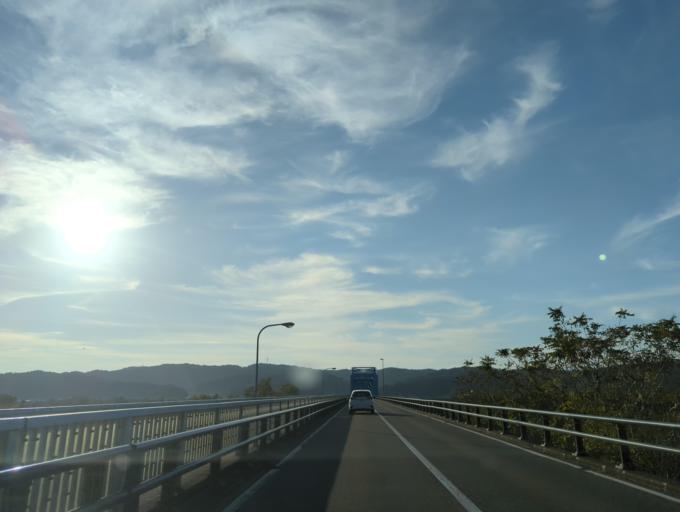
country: JP
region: Niigata
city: Nagaoka
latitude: 37.5534
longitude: 138.8264
